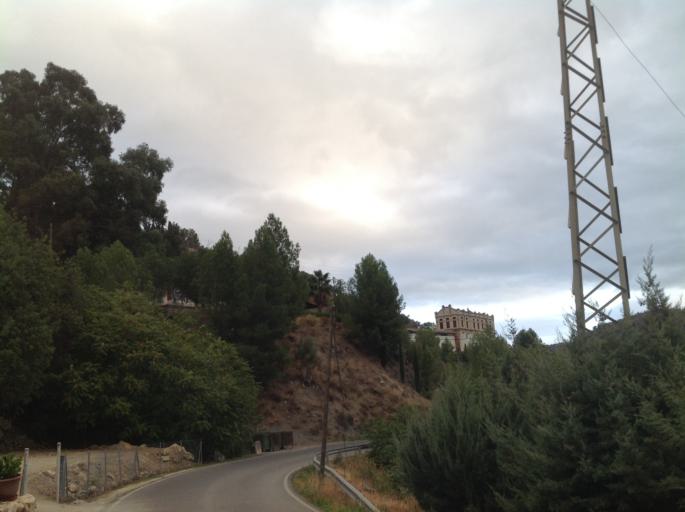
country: ES
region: Andalusia
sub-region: Provincia de Malaga
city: Carratraca
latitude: 36.9080
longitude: -4.7603
